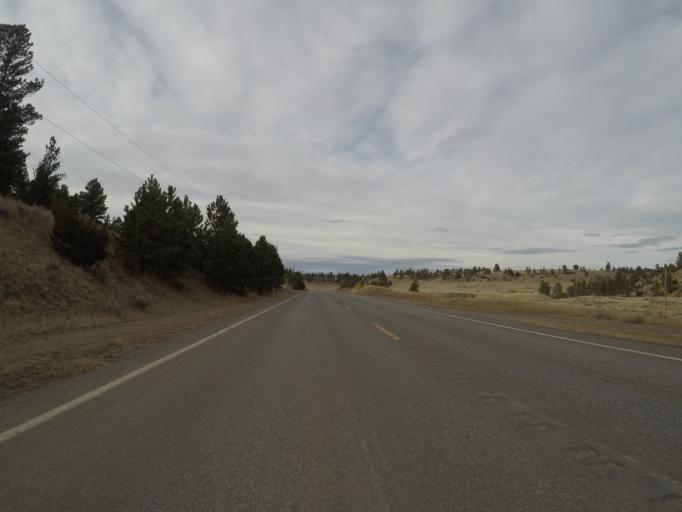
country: US
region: Montana
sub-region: Yellowstone County
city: Laurel
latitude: 45.8278
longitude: -108.7168
